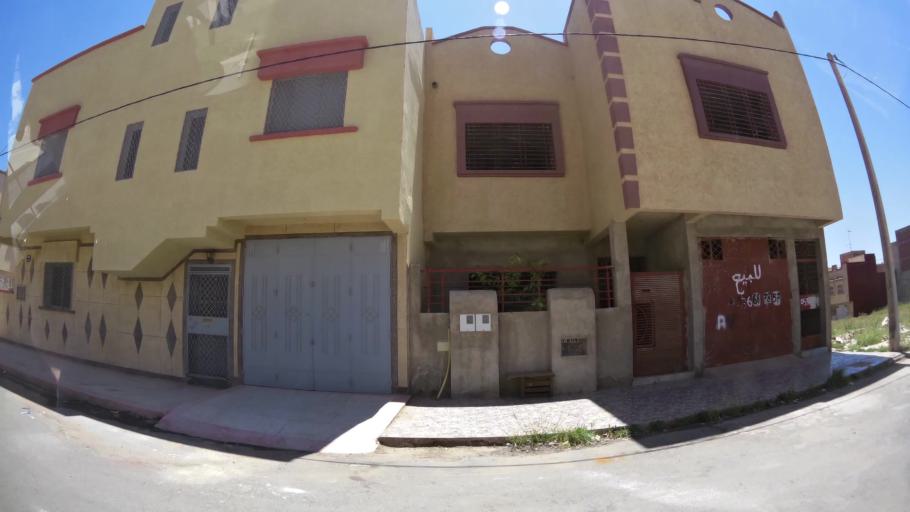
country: MA
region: Oriental
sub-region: Oujda-Angad
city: Oujda
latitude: 34.6644
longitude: -1.9217
